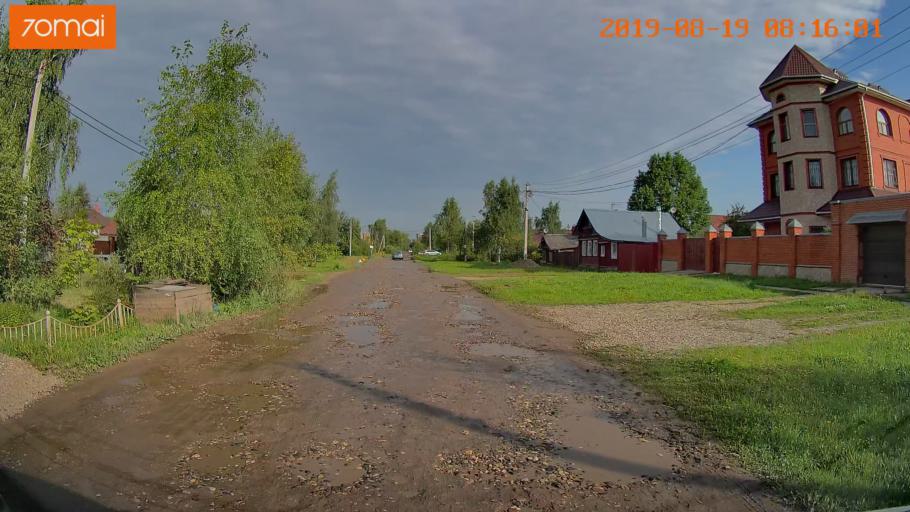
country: RU
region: Ivanovo
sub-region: Gorod Ivanovo
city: Ivanovo
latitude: 56.9741
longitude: 40.9997
